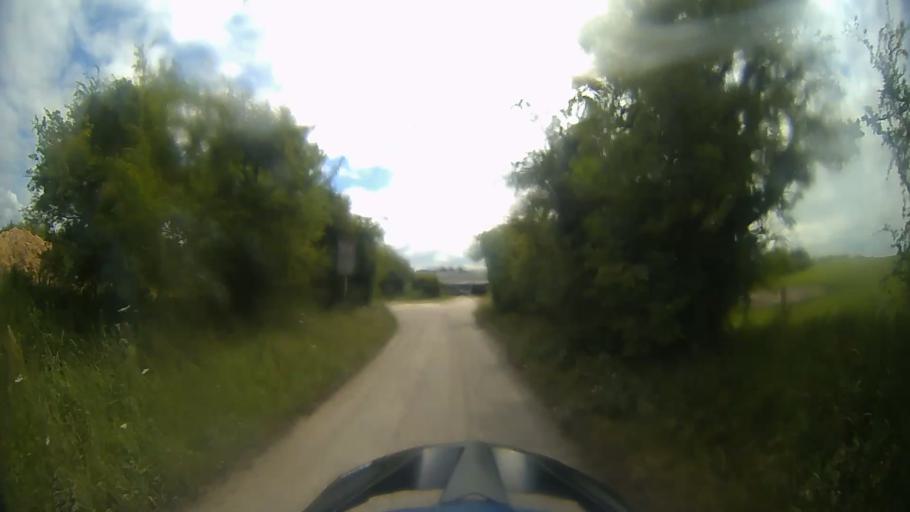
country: GB
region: England
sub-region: Oxfordshire
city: Wantage
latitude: 51.5555
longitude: -1.4479
